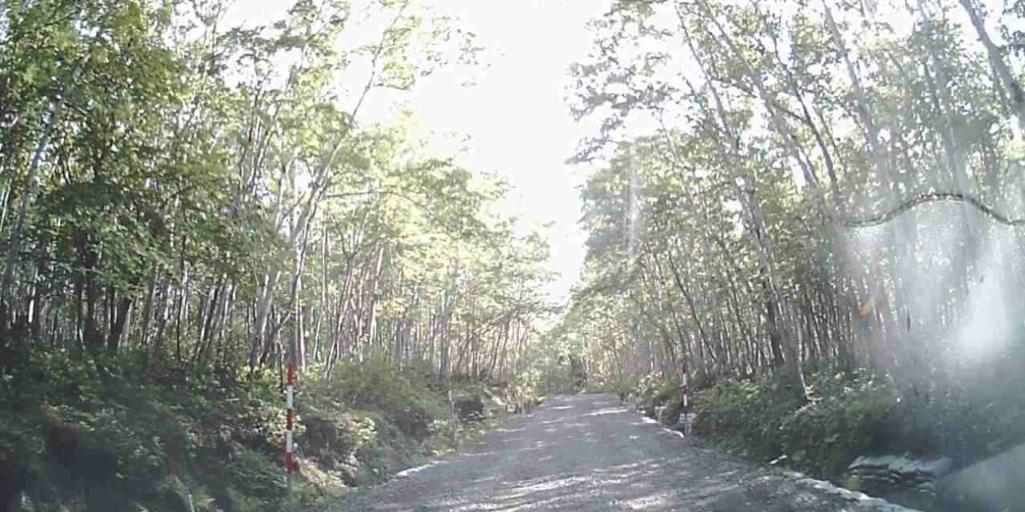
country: JP
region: Hokkaido
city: Shiraoi
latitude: 42.7060
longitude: 141.3956
